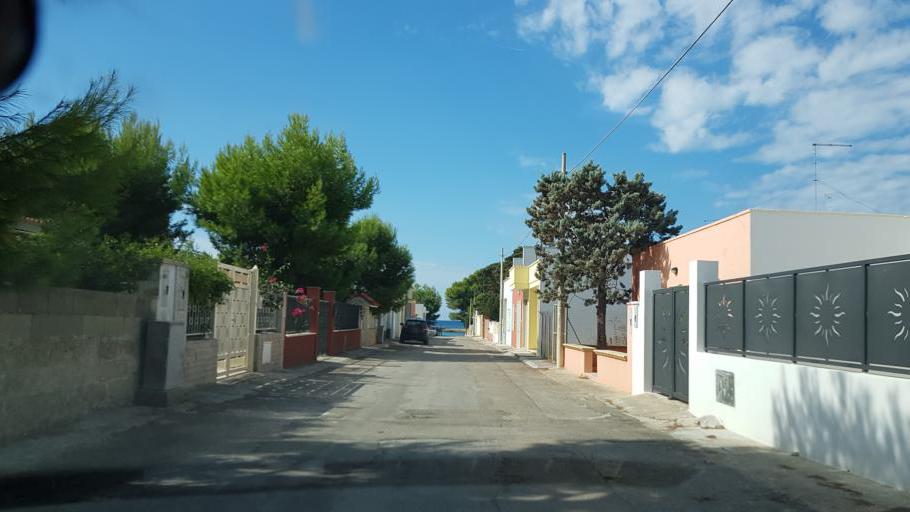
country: IT
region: Apulia
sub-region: Provincia di Lecce
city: Porto Cesareo
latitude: 40.2354
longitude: 17.9155
